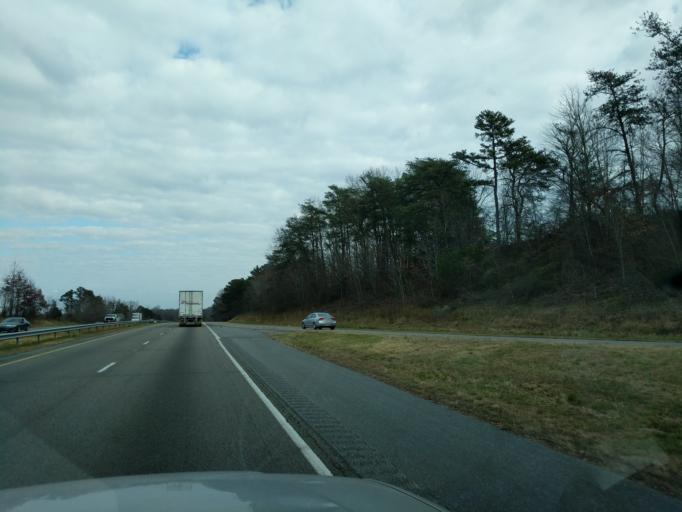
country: US
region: North Carolina
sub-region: Burke County
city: Glen Alpine
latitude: 35.6913
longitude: -81.8183
